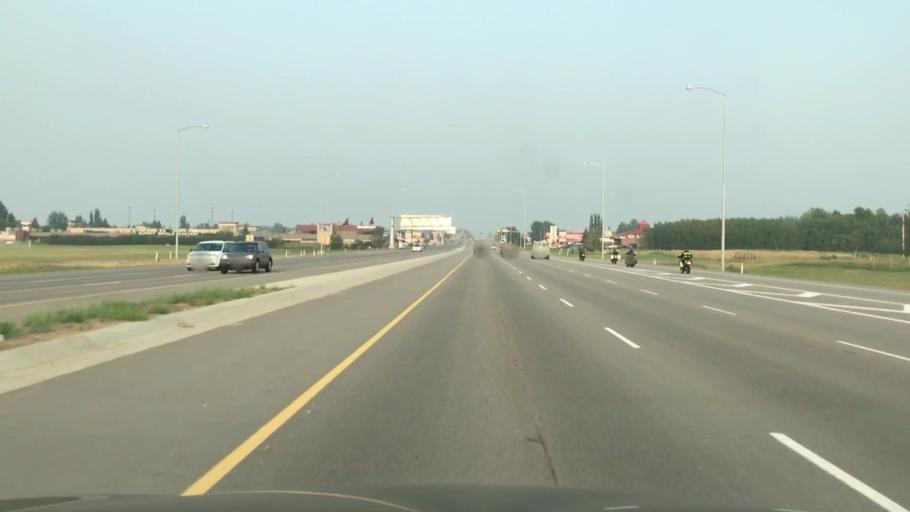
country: CA
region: Alberta
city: Sherwood Park
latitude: 53.5120
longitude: -113.3368
